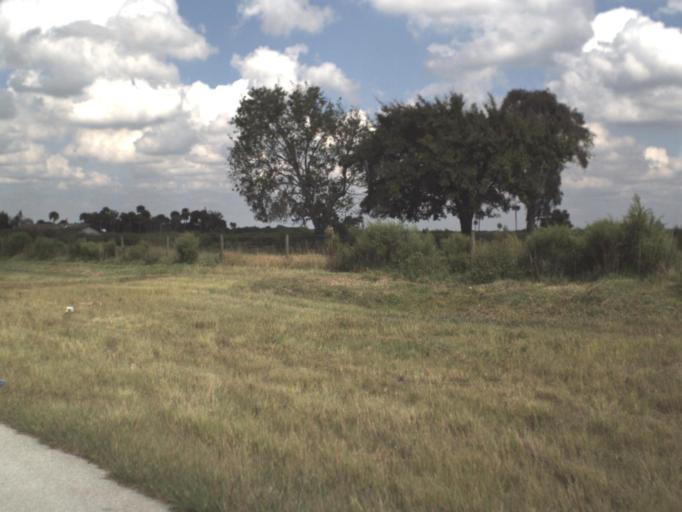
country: US
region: Florida
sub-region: Okeechobee County
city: Okeechobee
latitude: 27.3078
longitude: -80.9022
